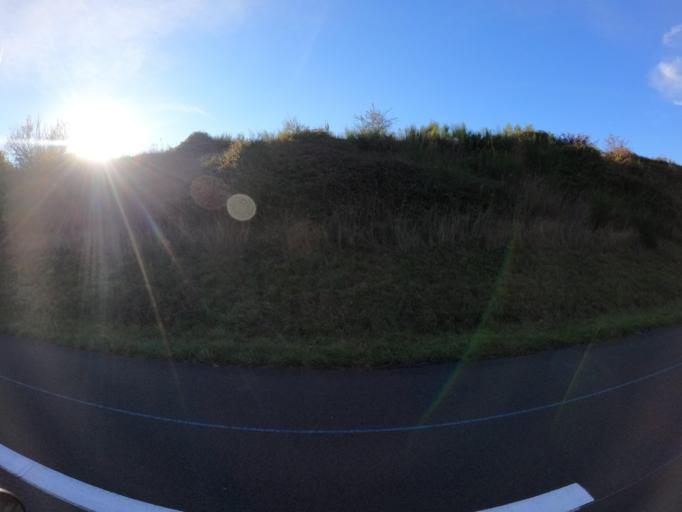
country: FR
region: Pays de la Loire
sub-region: Departement de Maine-et-Loire
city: Chemille-Melay
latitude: 47.2172
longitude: -0.7624
